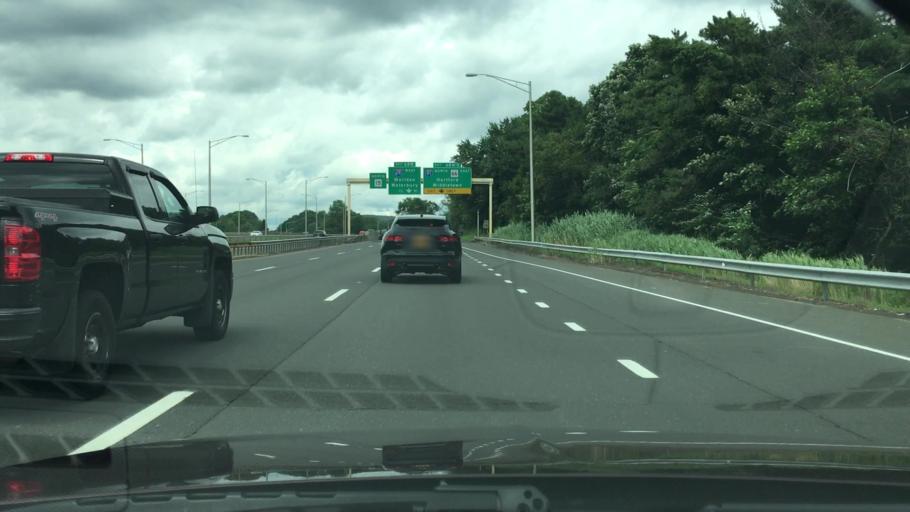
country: US
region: Connecticut
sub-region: New Haven County
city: Meriden
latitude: 41.5279
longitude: -72.7693
